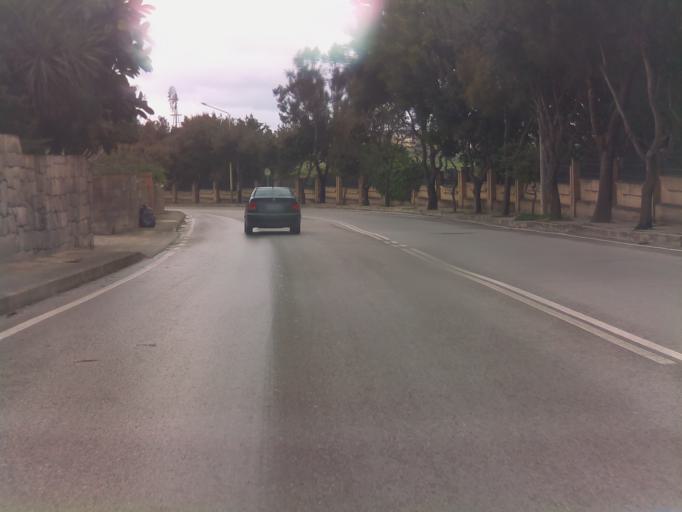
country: MT
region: Il-Mosta
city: Mosta
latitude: 35.9171
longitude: 14.4168
